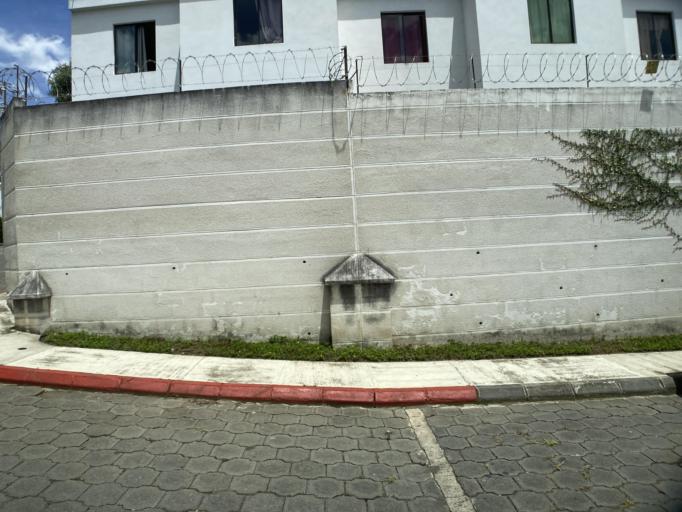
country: GT
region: Sacatepequez
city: Ciudad Vieja
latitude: 14.5238
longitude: -90.7469
